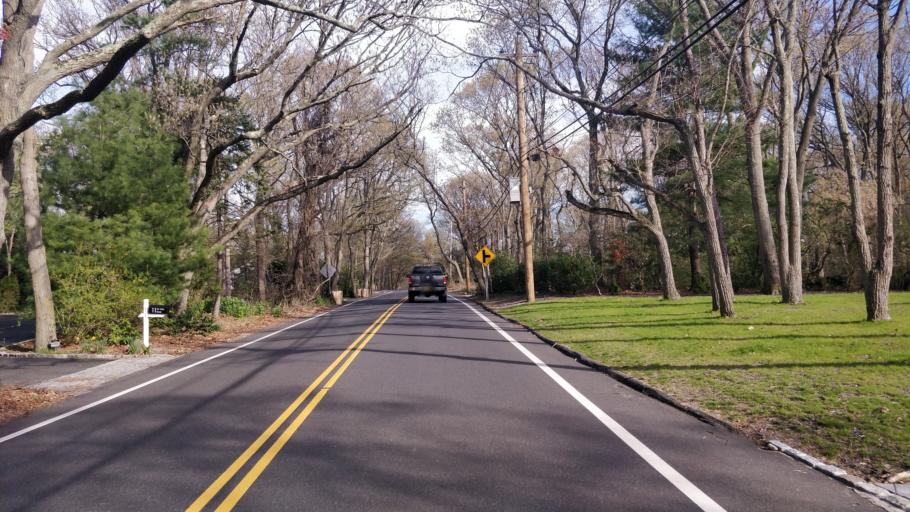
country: US
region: New York
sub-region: Suffolk County
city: Stony Brook
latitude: 40.9411
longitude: -73.1327
